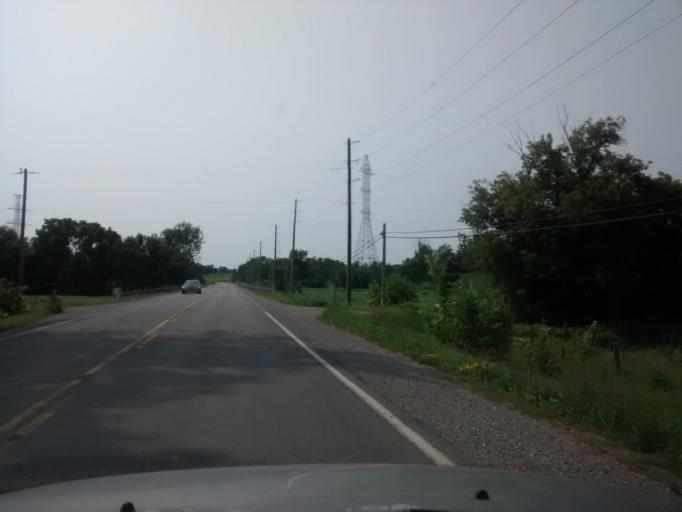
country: CA
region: Ontario
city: Ancaster
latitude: 43.0603
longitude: -79.9178
